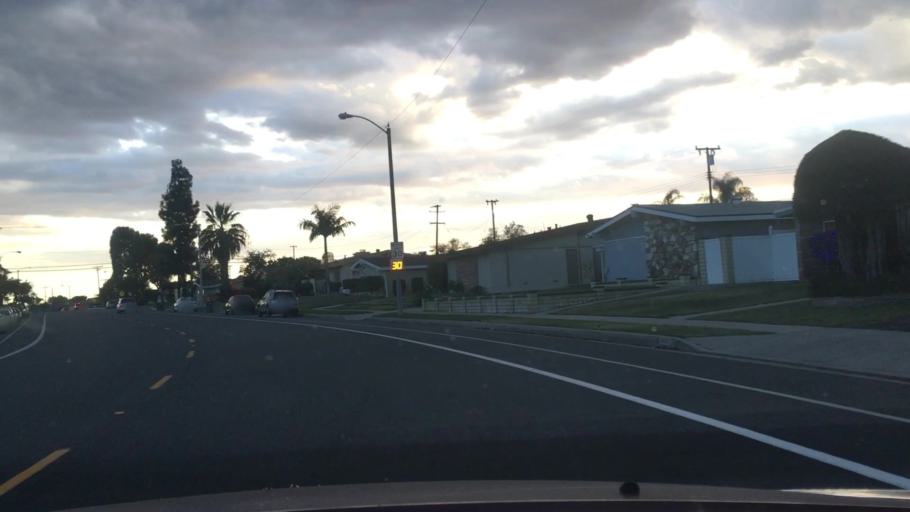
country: US
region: California
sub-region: Los Angeles County
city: La Mirada
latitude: 33.9135
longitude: -118.0203
